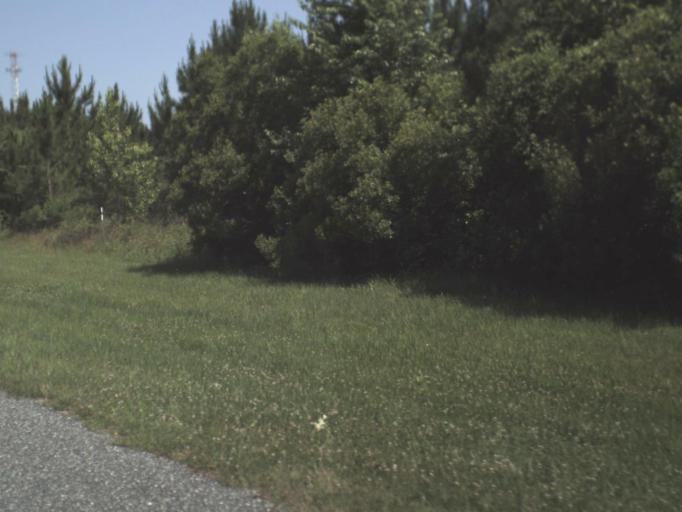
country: US
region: Florida
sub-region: Clay County
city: Middleburg
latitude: 29.9793
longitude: -81.9288
